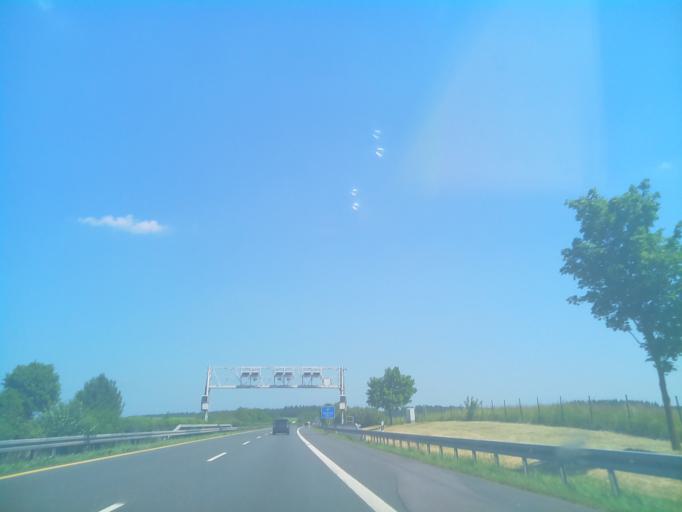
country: DE
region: Bavaria
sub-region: Regierungsbezirk Unterfranken
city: Kleinrinderfeld
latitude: 49.6971
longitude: 9.7927
